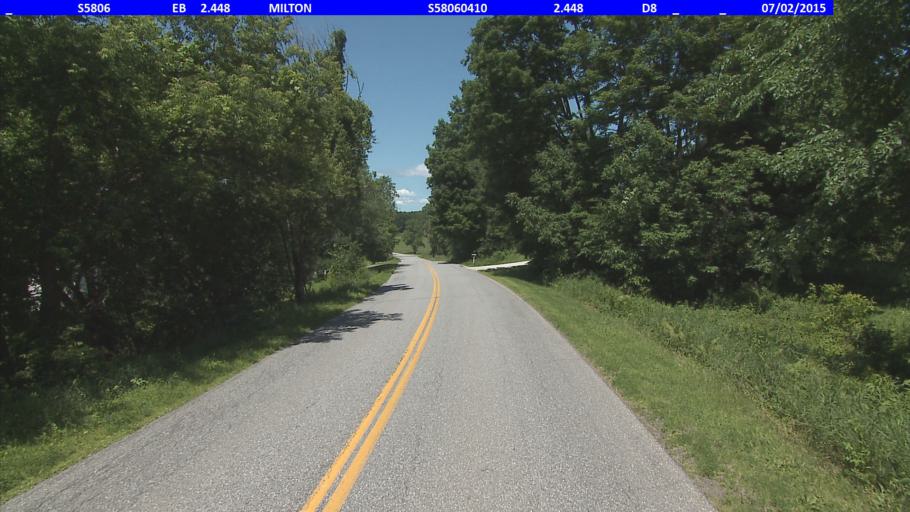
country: US
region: Vermont
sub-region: Chittenden County
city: Milton
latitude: 44.6655
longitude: -73.1569
